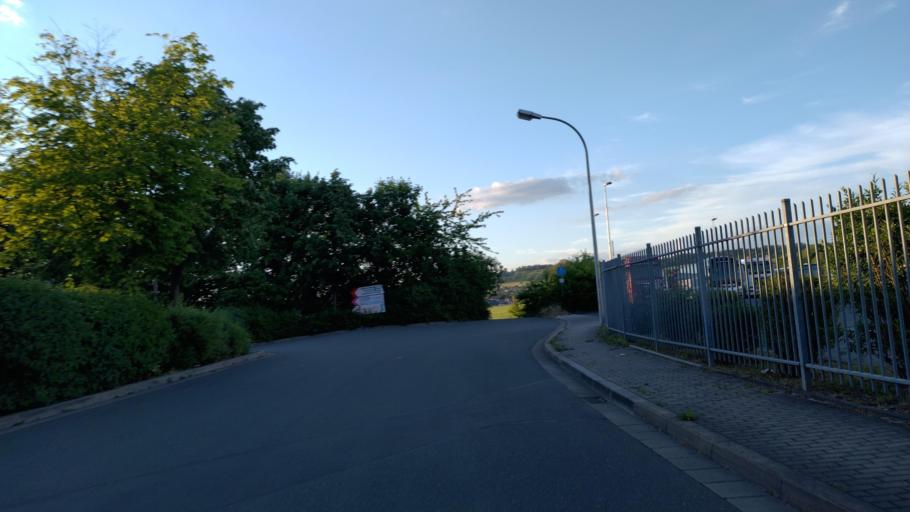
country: DE
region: Bavaria
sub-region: Upper Franconia
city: Bindlach
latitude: 49.9692
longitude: 11.6078
